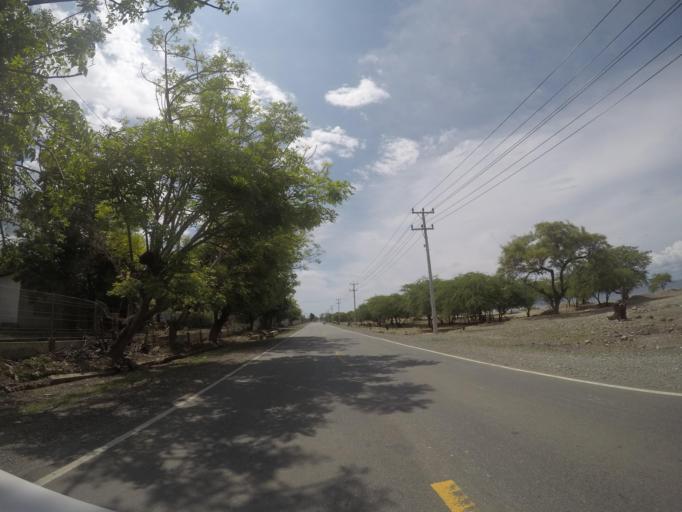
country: TL
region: Liquica
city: Liquica
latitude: -8.5643
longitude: 125.4074
